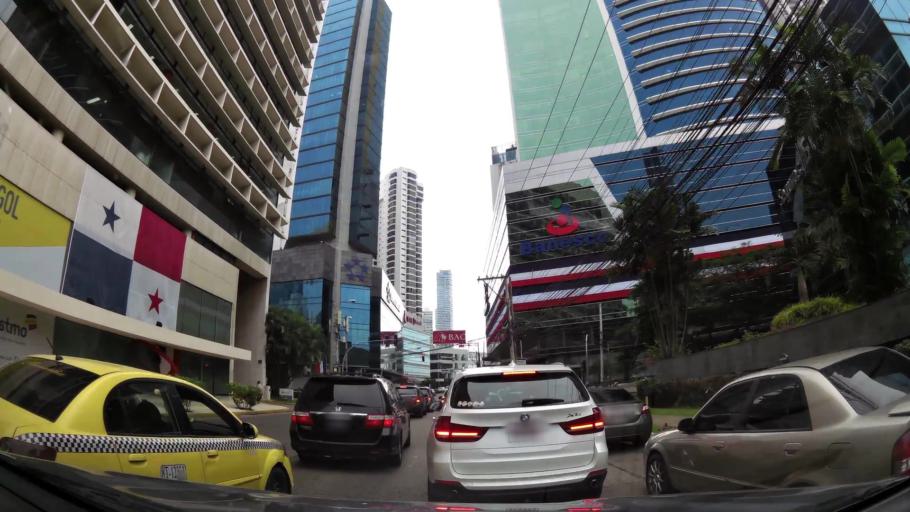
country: PA
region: Panama
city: Panama
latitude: 8.9777
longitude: -79.5229
